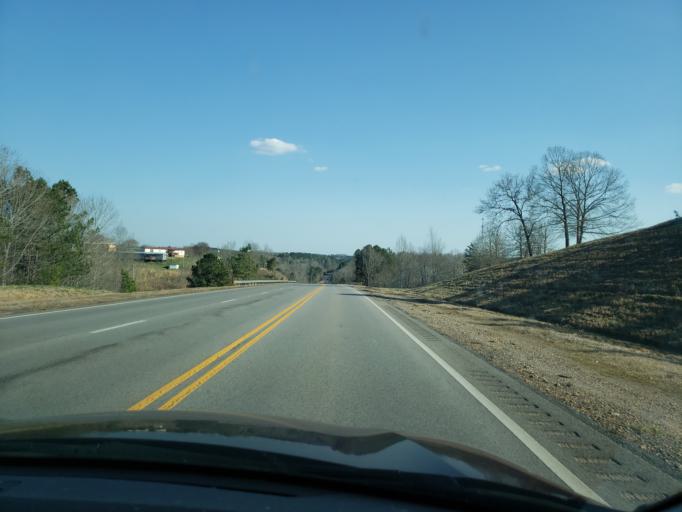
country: US
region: Alabama
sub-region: Cleburne County
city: Heflin
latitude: 33.4823
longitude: -85.5912
